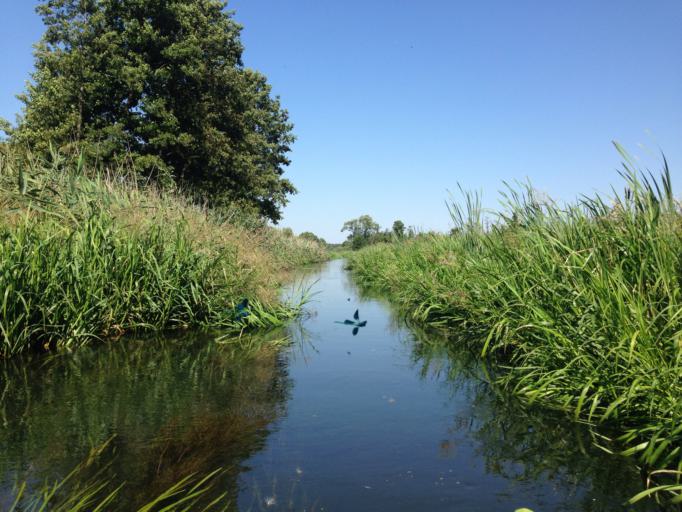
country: PL
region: Kujawsko-Pomorskie
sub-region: Powiat brodnicki
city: Bartniczka
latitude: 53.2672
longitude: 19.5946
